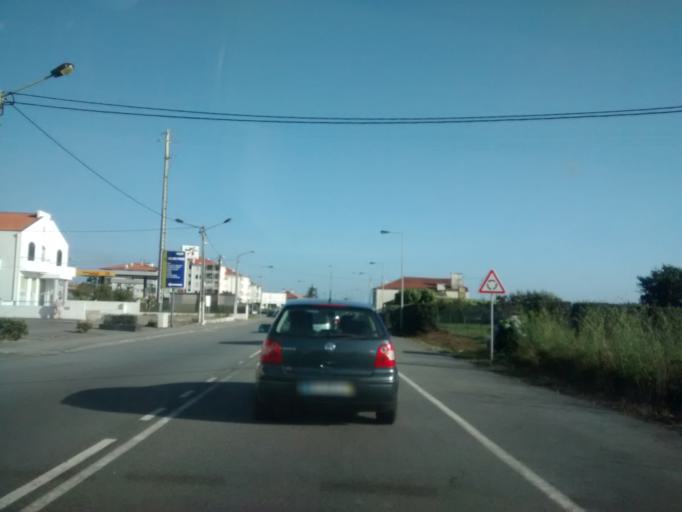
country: PT
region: Viana do Castelo
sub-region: Viana do Castelo
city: Areosa
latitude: 41.7252
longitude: -8.8600
